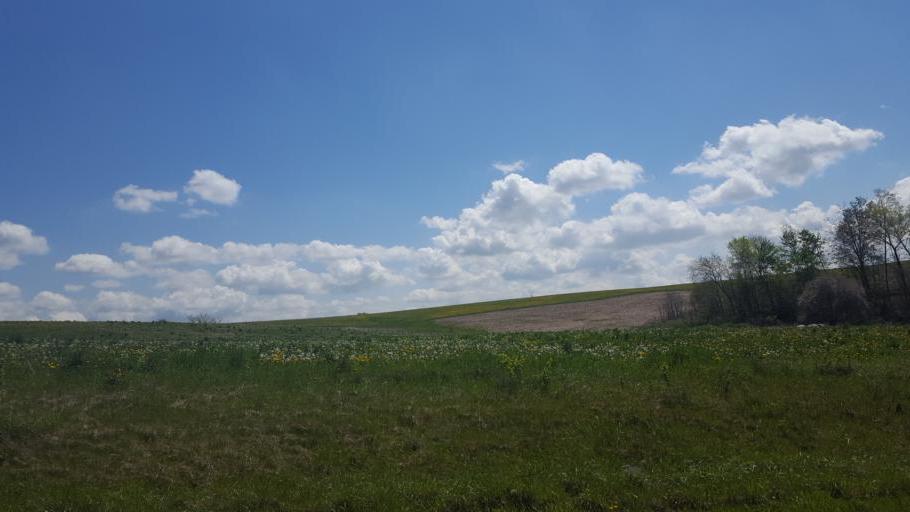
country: US
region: Wisconsin
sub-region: Vernon County
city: Hillsboro
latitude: 43.5811
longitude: -90.3618
